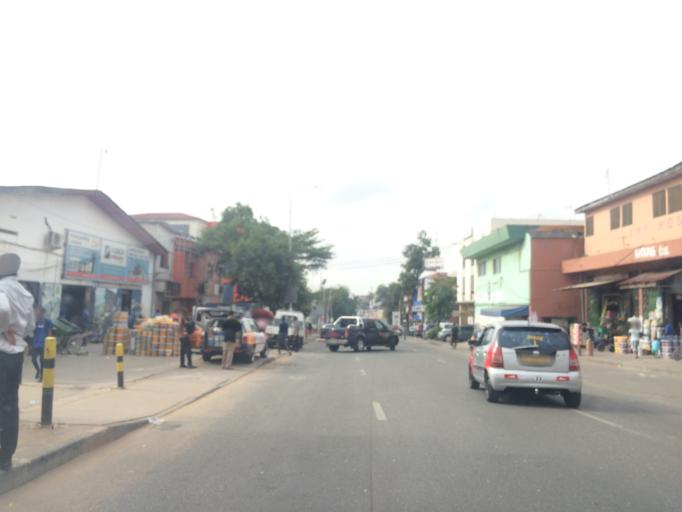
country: GH
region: Greater Accra
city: Accra
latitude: 5.5536
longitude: -0.2085
